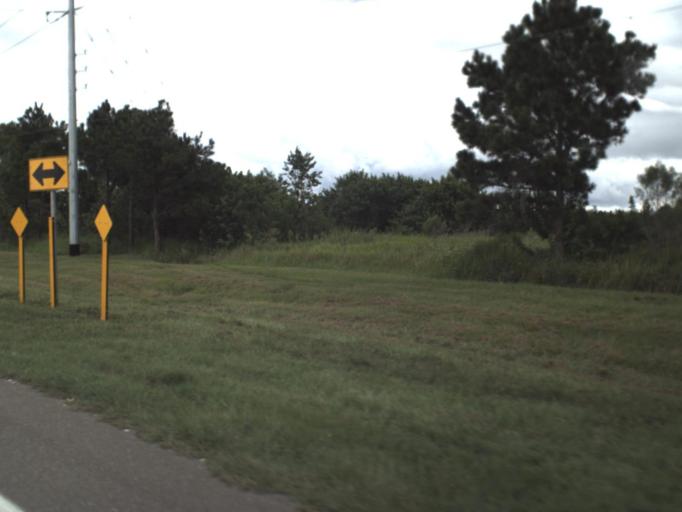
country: US
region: Florida
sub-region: Polk County
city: Mulberry
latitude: 27.7046
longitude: -82.0203
